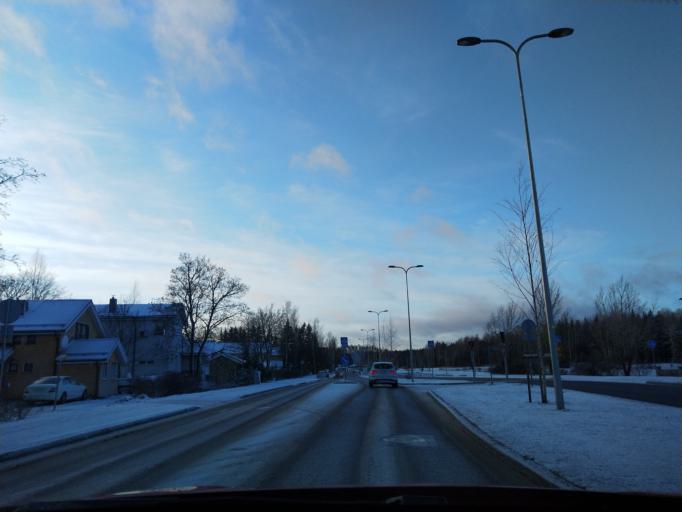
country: FI
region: Uusimaa
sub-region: Helsinki
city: Helsinki
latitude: 60.2559
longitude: 24.9335
